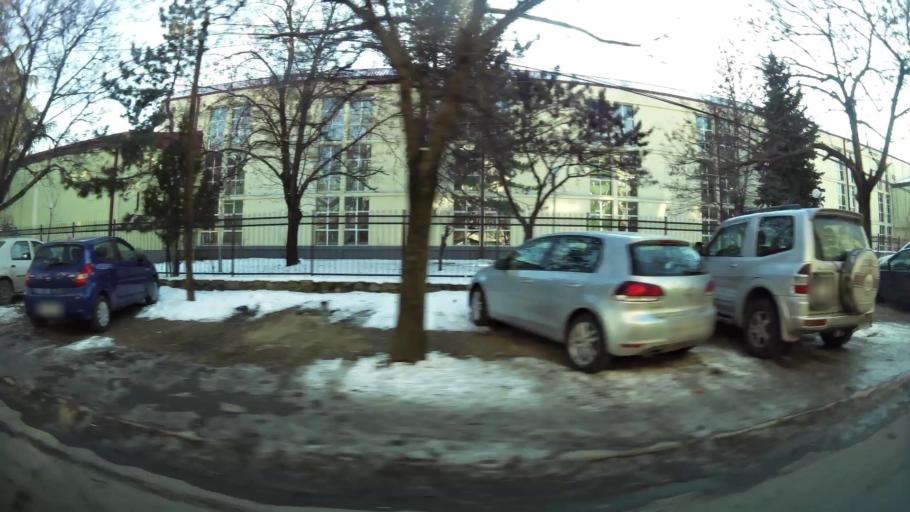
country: MK
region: Karpos
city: Skopje
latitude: 42.0002
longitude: 21.4019
